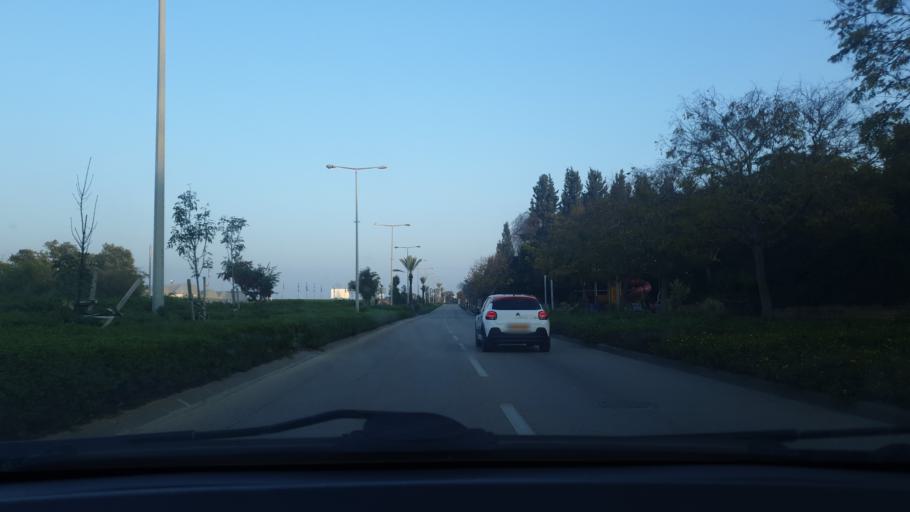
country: IL
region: Central District
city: Bet Dagan
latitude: 31.9735
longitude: 34.8185
